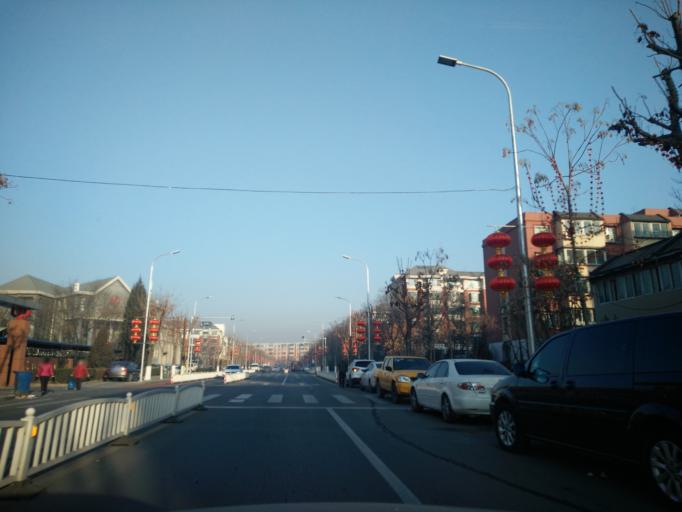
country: CN
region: Beijing
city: Jiugong
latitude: 39.7961
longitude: 116.4728
